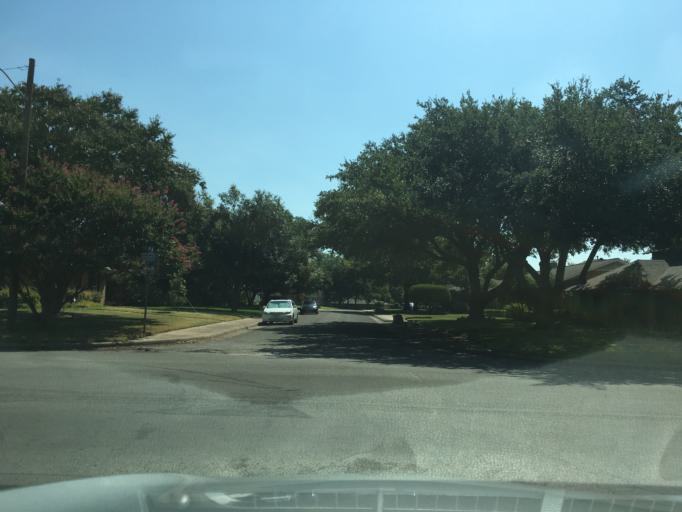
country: US
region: Texas
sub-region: Dallas County
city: Garland
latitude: 32.8594
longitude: -96.6930
